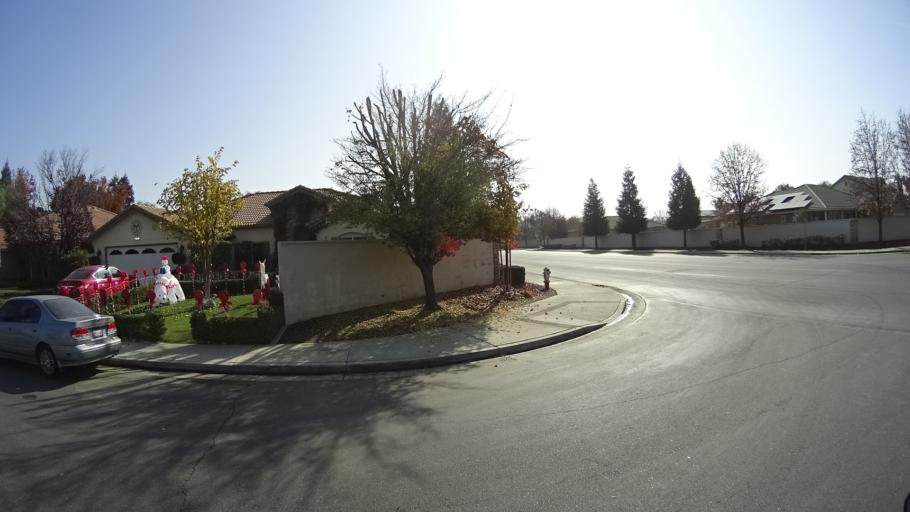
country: US
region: California
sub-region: Kern County
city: Greenacres
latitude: 35.4245
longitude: -119.1178
